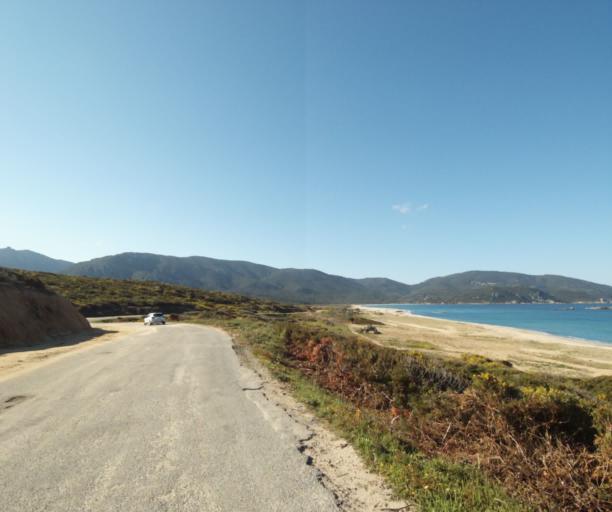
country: FR
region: Corsica
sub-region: Departement de la Corse-du-Sud
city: Propriano
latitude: 41.6694
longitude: 8.8830
